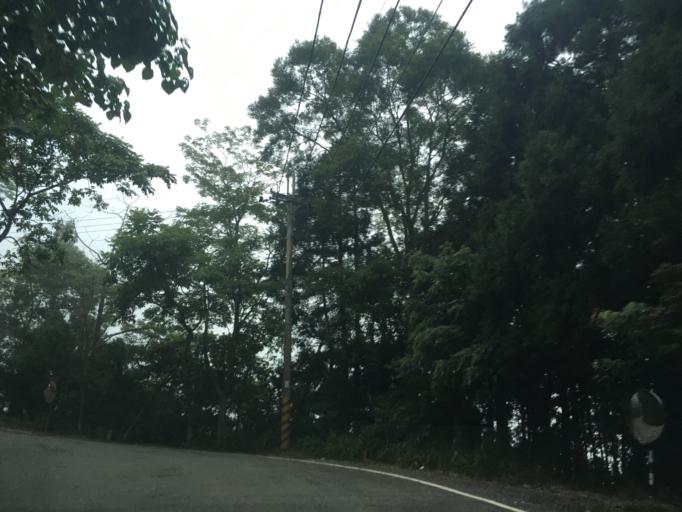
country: TW
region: Taiwan
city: Fengyuan
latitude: 24.2439
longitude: 120.9261
